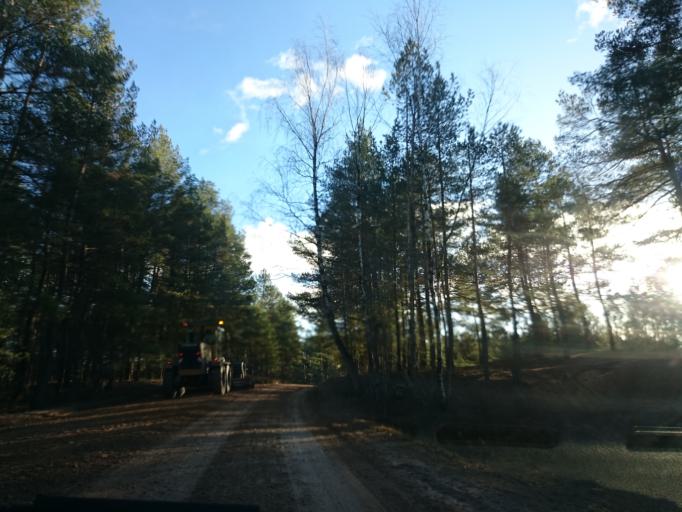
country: LV
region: Garkalne
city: Garkalne
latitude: 57.0591
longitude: 24.4155
